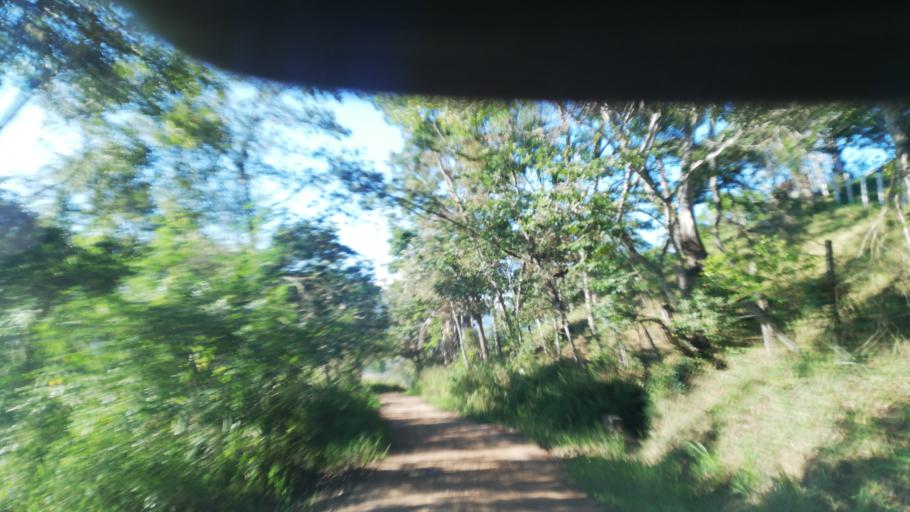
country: CO
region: Cundinamarca
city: Viani
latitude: 4.8367
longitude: -74.6228
